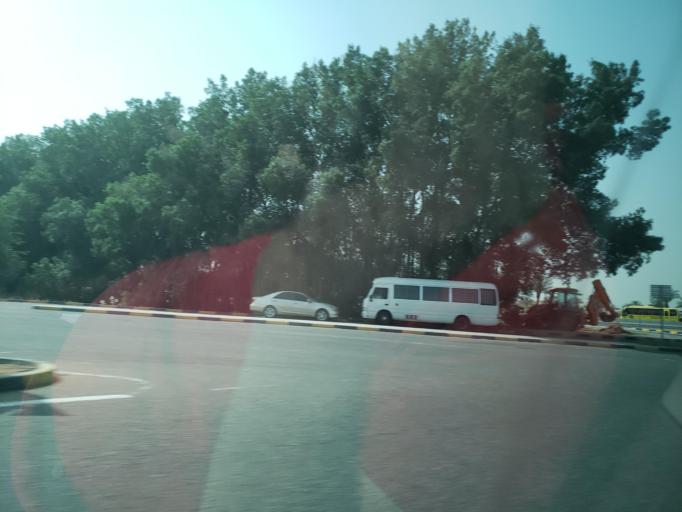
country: AE
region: Ash Shariqah
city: Sharjah
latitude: 25.3218
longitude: 55.5044
